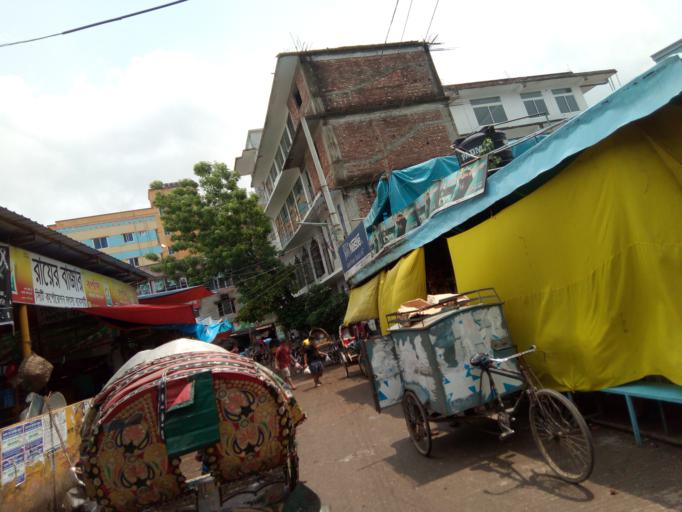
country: BD
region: Dhaka
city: Azimpur
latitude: 23.7460
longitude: 90.3636
